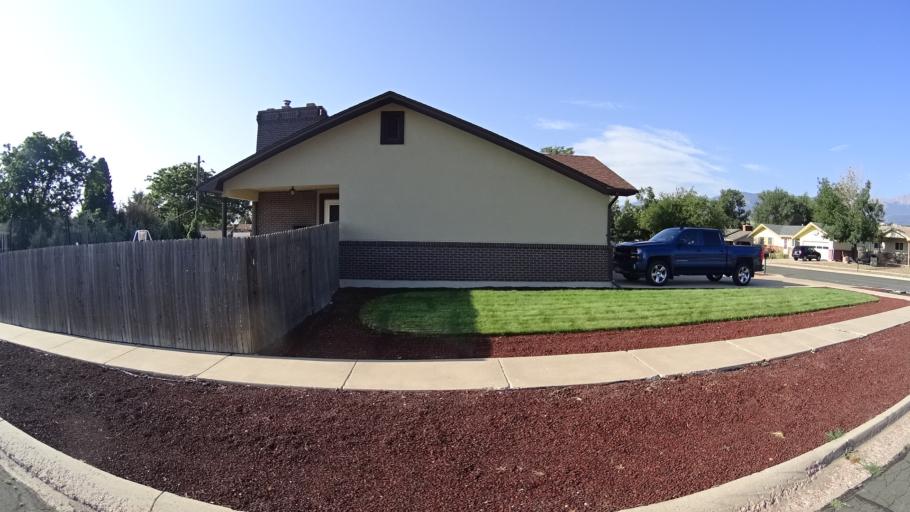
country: US
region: Colorado
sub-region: El Paso County
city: Colorado Springs
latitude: 38.8909
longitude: -104.8396
